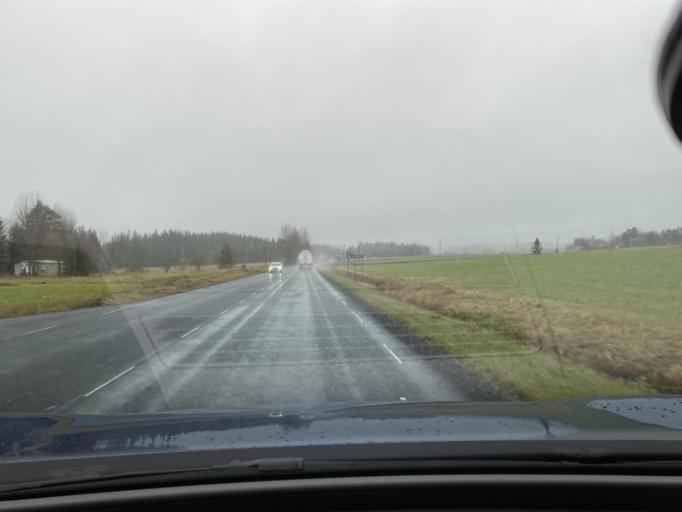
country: FI
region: Haeme
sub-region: Forssa
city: Ypaejae
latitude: 60.7770
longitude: 23.3189
